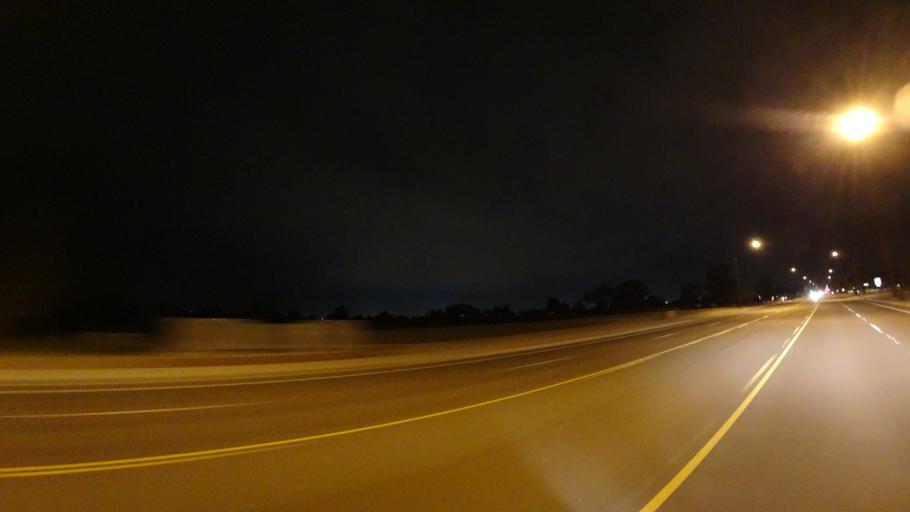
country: US
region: Arizona
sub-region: Maricopa County
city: Queen Creek
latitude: 33.2568
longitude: -111.7380
